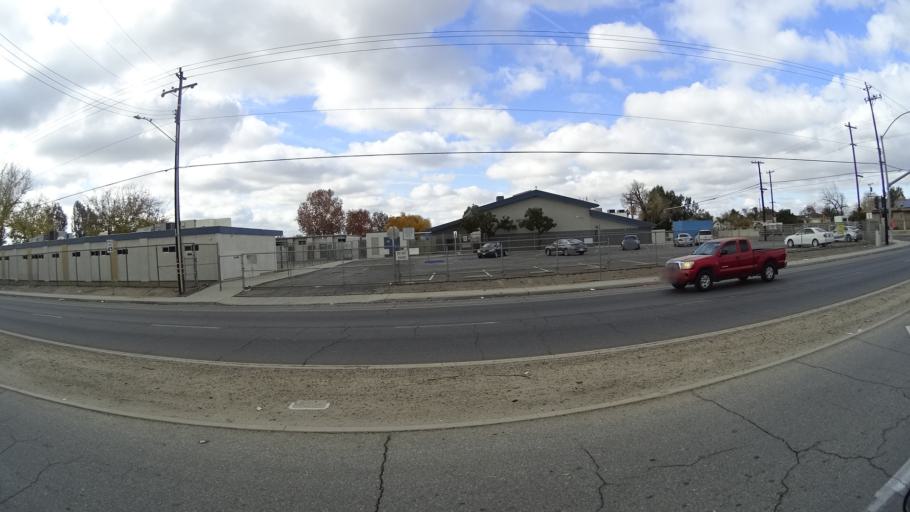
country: US
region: California
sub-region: Kern County
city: Bakersfield
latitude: 35.3645
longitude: -118.9675
